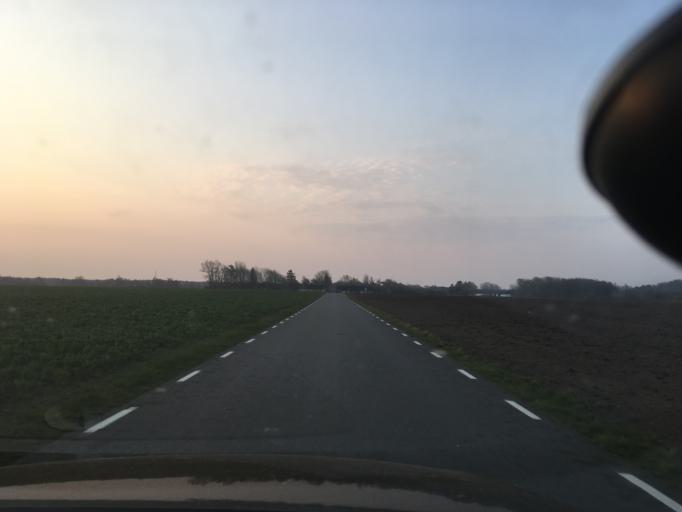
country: SE
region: Skane
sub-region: Ystads Kommun
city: Kopingebro
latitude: 55.4050
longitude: 14.1591
